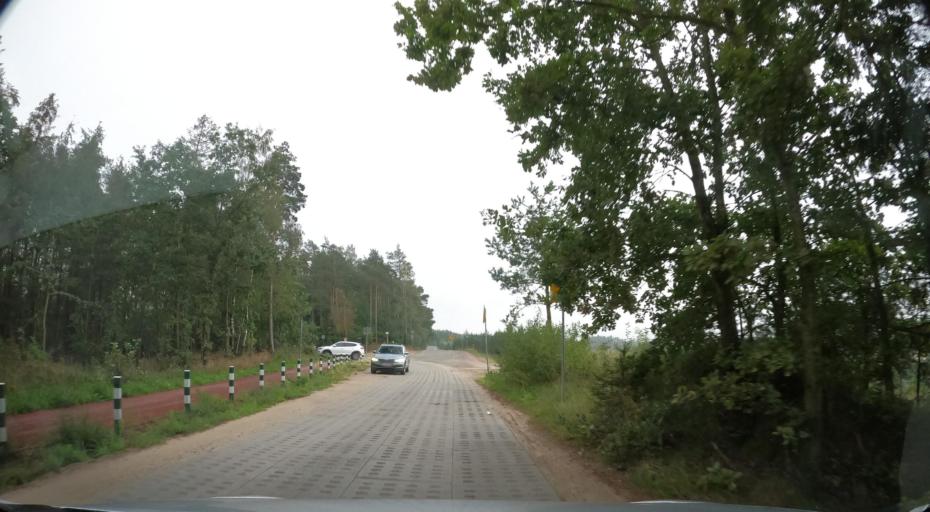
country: PL
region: Pomeranian Voivodeship
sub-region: Powiat kartuski
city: Chwaszczyno
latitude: 54.4226
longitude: 18.4156
